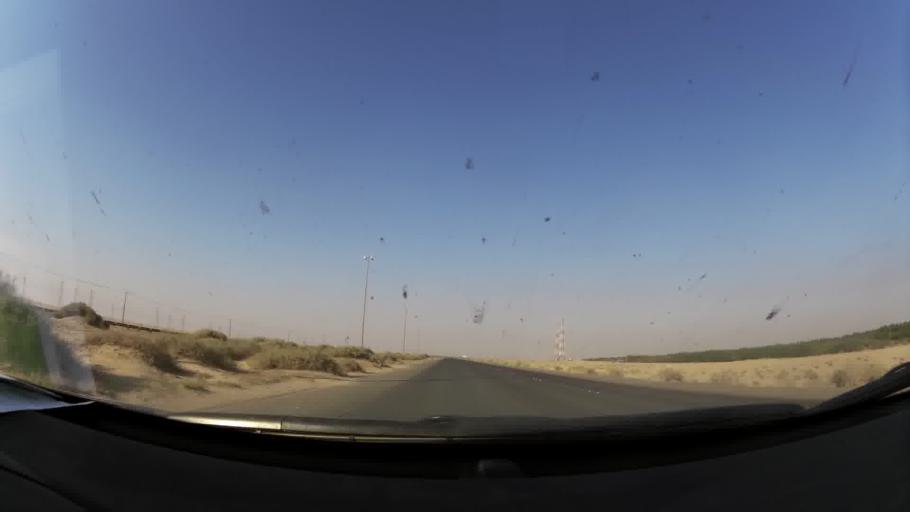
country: IQ
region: Basra Governorate
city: Umm Qasr
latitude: 30.0118
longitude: 47.6508
